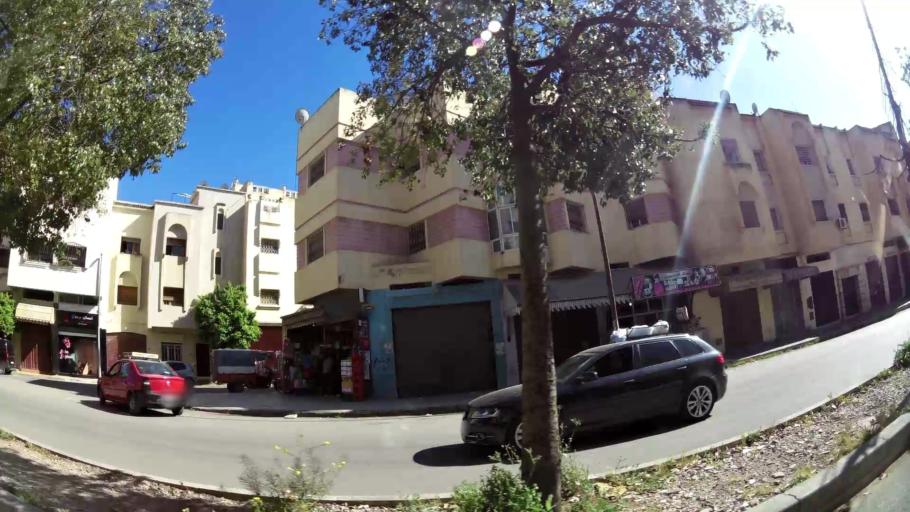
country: MA
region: Fes-Boulemane
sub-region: Fes
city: Fes
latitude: 34.0133
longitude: -4.9804
